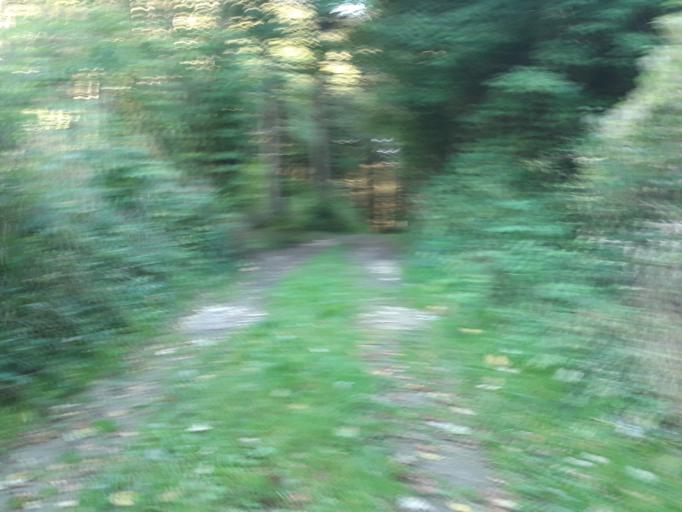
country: DE
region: North Rhine-Westphalia
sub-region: Regierungsbezirk Detmold
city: Schlangen
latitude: 51.7849
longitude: 8.8760
